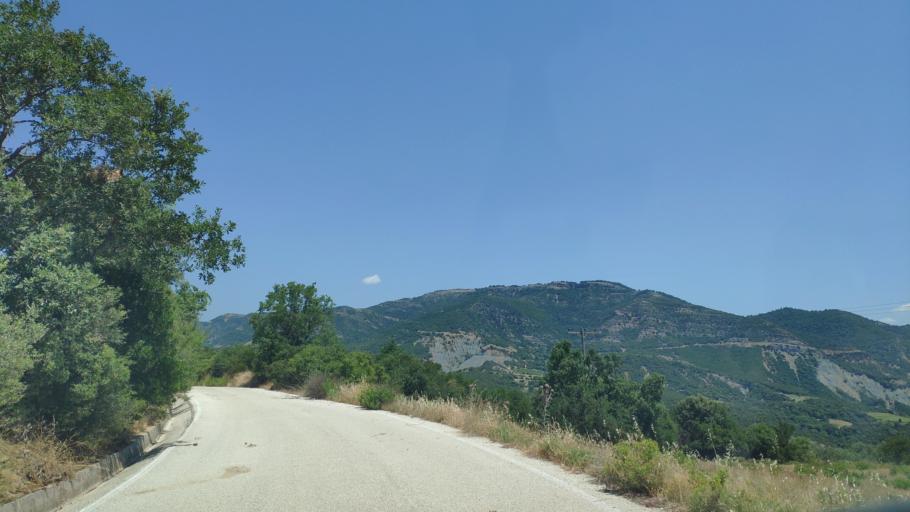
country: GR
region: West Greece
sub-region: Nomos Aitolias kai Akarnanias
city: Sardinia
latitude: 38.8806
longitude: 21.2801
